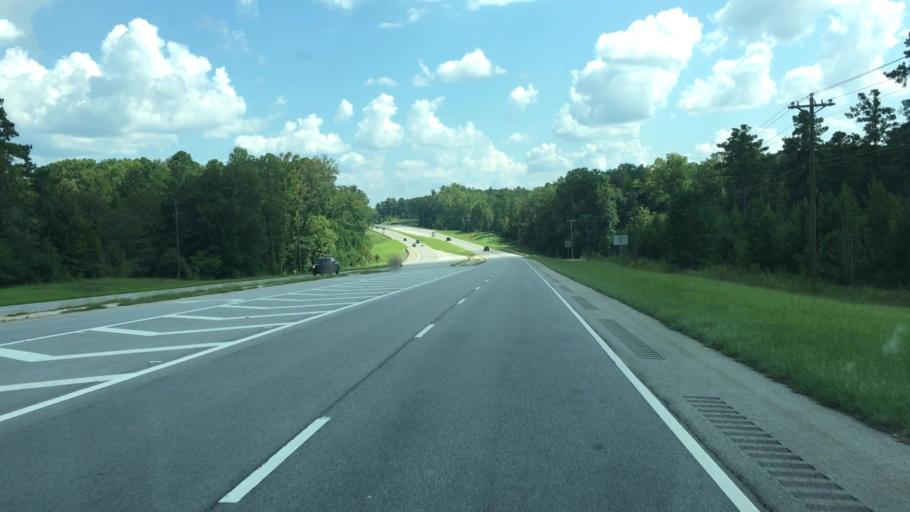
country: US
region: Georgia
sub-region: Putnam County
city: Eatonton
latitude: 33.2435
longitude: -83.3235
